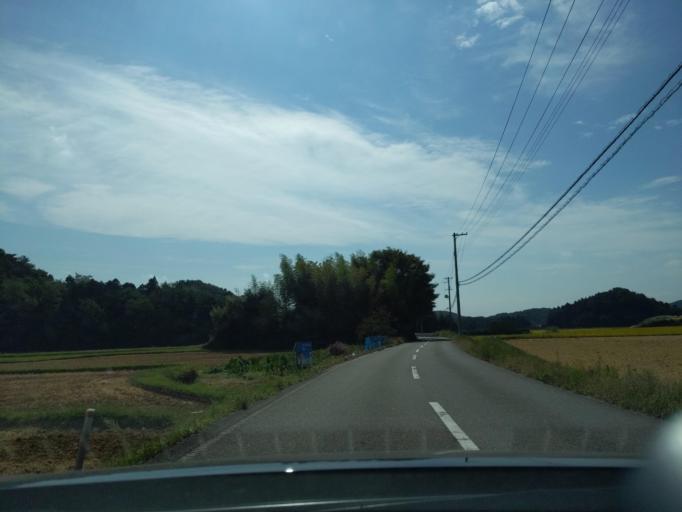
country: JP
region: Fukushima
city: Koriyama
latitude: 37.3838
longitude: 140.2610
